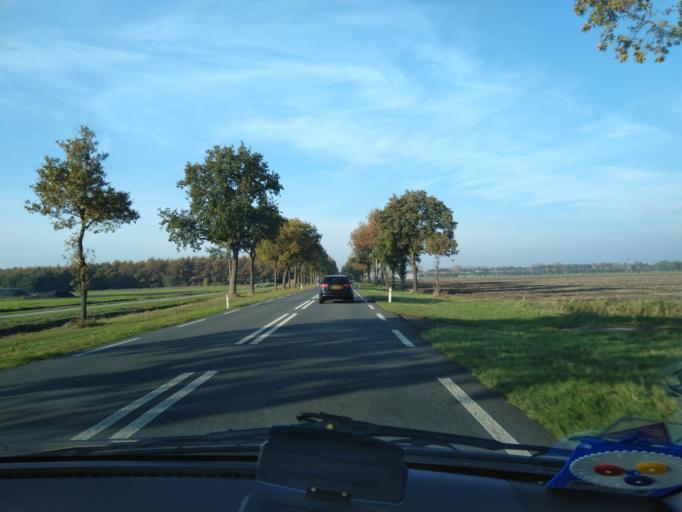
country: NL
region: Groningen
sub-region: Gemeente Hoogezand-Sappemeer
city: Hoogezand
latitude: 53.1415
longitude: 6.7688
